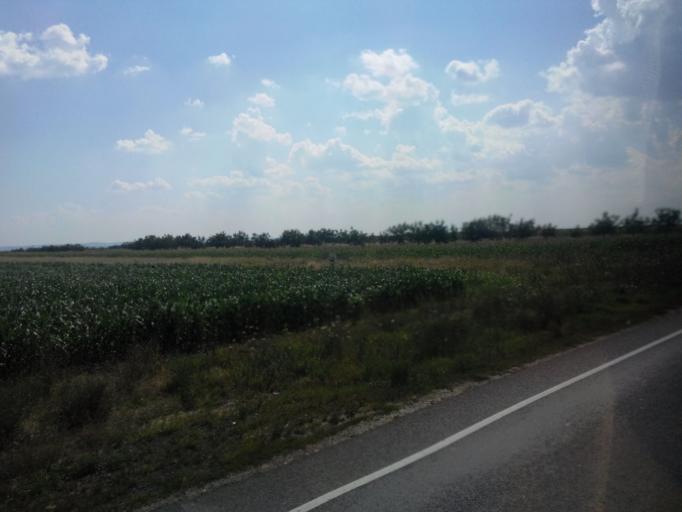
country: RO
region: Timis
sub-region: Comuna Costeiu
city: Costeiu
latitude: 45.7438
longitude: 21.8137
